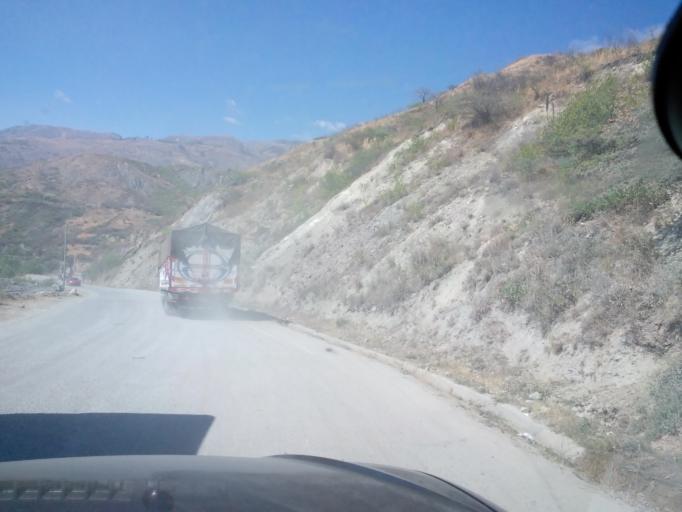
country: PE
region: Apurimac
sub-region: Provincia de Abancay
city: Curahuasi
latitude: -13.5442
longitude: -72.6773
